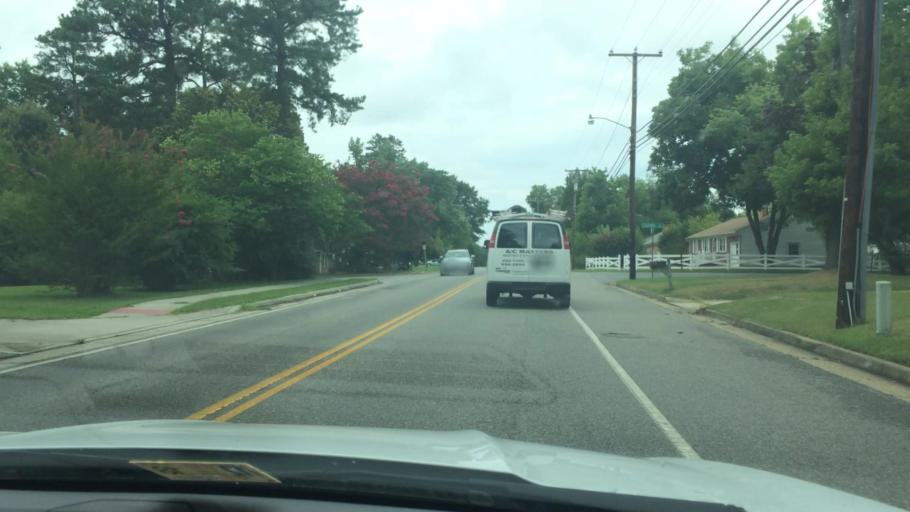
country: US
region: Virginia
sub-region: City of Williamsburg
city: Williamsburg
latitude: 37.2706
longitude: -76.6721
